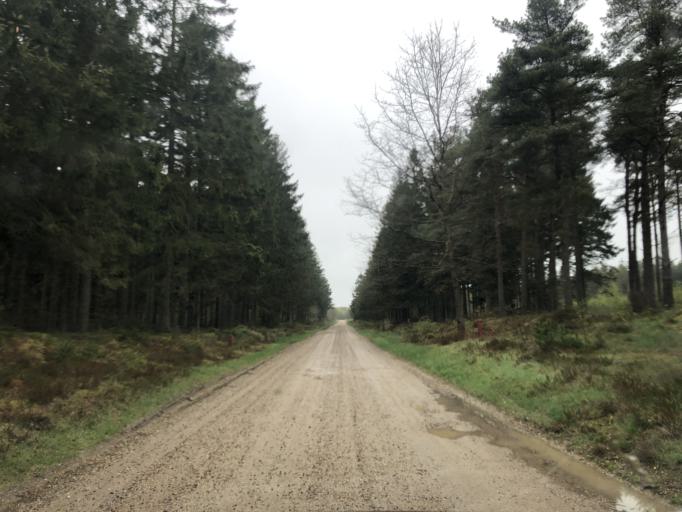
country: DK
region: Central Jutland
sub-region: Lemvig Kommune
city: Lemvig
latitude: 56.4797
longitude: 8.3700
